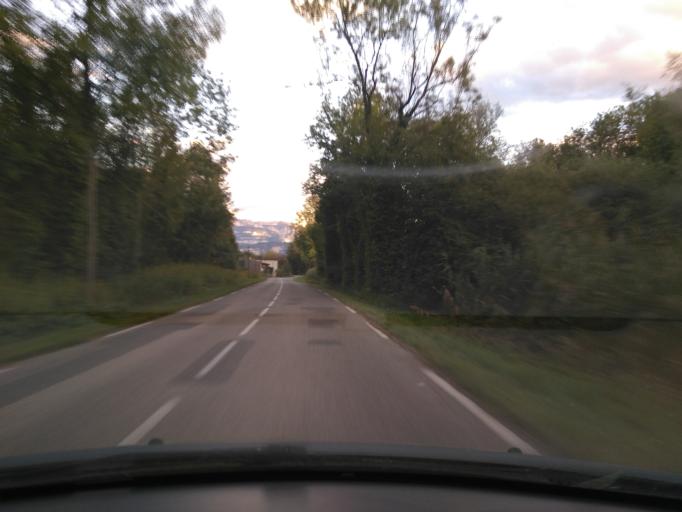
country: FR
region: Rhone-Alpes
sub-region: Departement de l'Isere
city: Saint-Cassien
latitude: 45.3681
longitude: 5.5438
